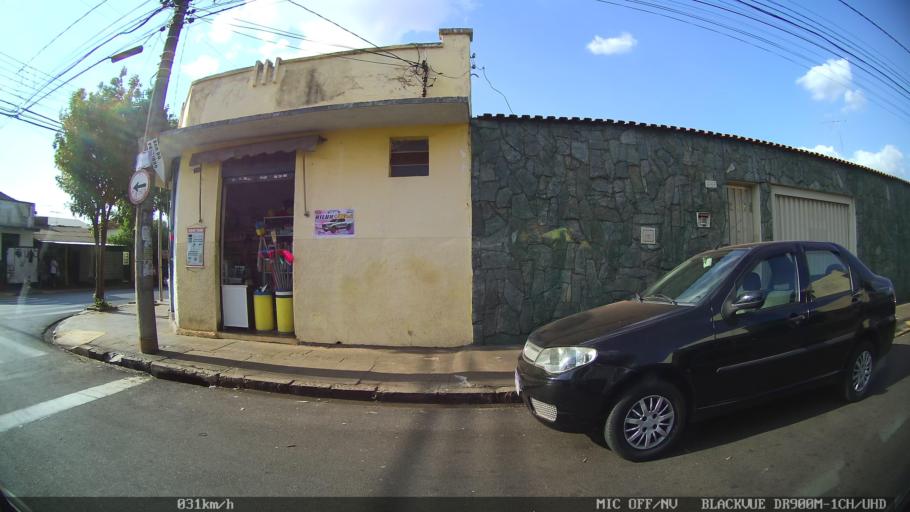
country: BR
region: Sao Paulo
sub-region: Ribeirao Preto
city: Ribeirao Preto
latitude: -21.1630
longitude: -47.8082
